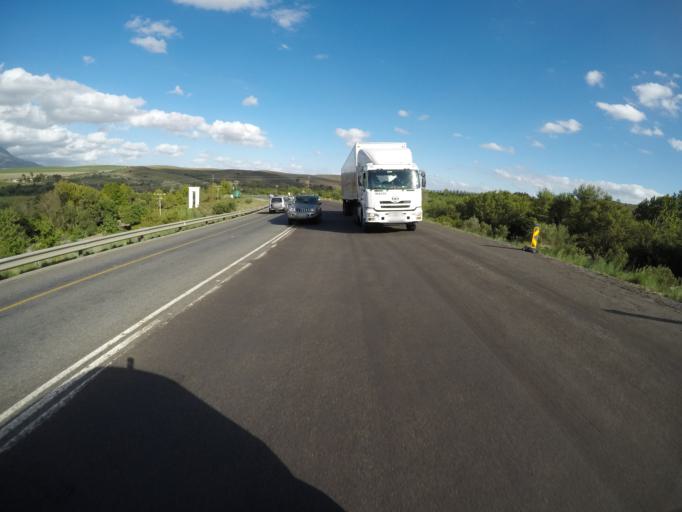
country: ZA
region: Western Cape
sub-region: Cape Winelands District Municipality
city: Ashton
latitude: -33.9458
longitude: 20.2152
